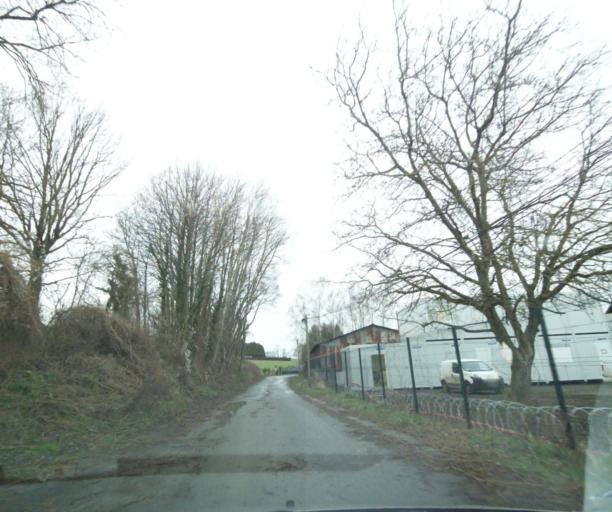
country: FR
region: Picardie
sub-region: Departement de l'Oise
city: Noyon
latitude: 49.5767
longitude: 2.9755
